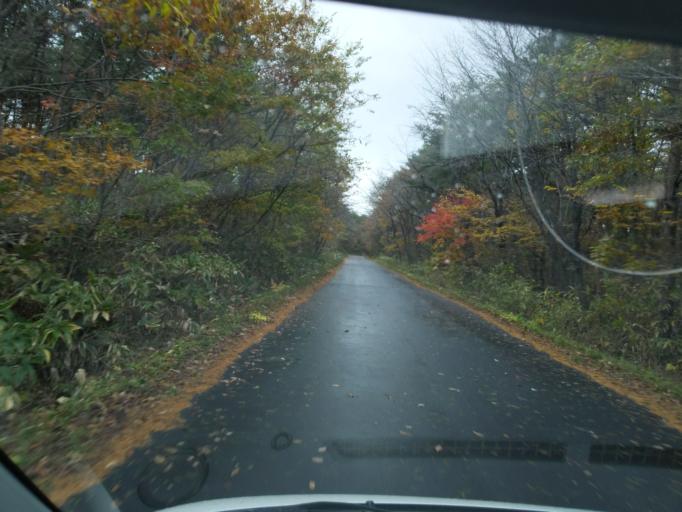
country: JP
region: Iwate
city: Mizusawa
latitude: 39.0767
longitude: 141.0253
